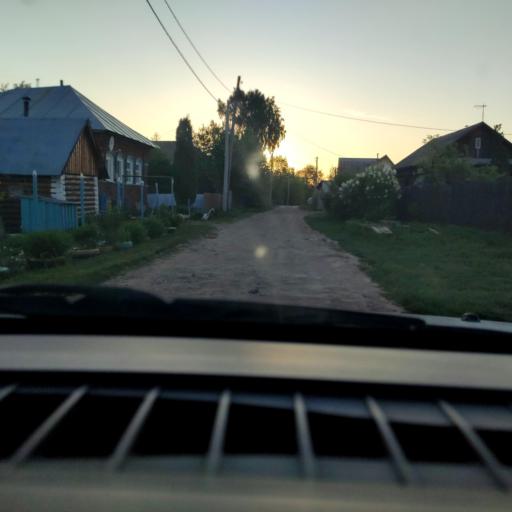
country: RU
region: Perm
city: Froly
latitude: 57.9290
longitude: 56.2848
